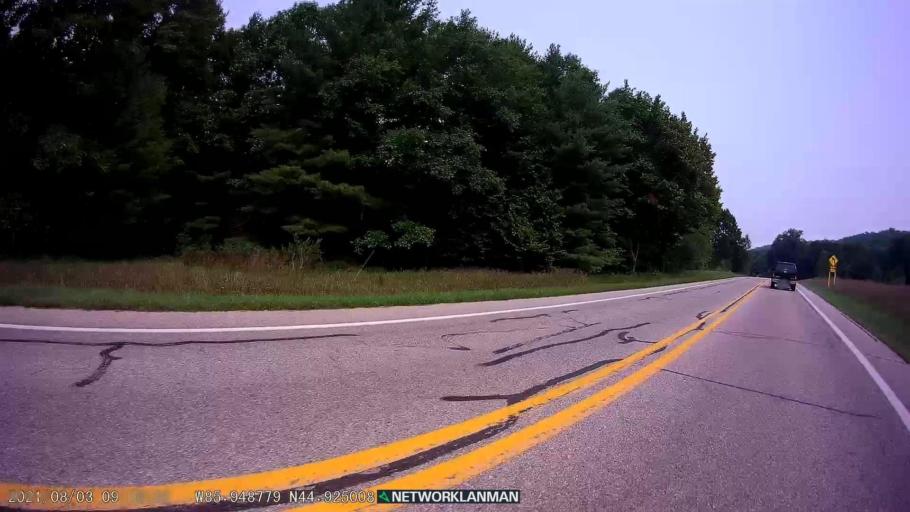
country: US
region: Michigan
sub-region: Leelanau County
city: Leland
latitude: 44.9253
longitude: -85.9484
